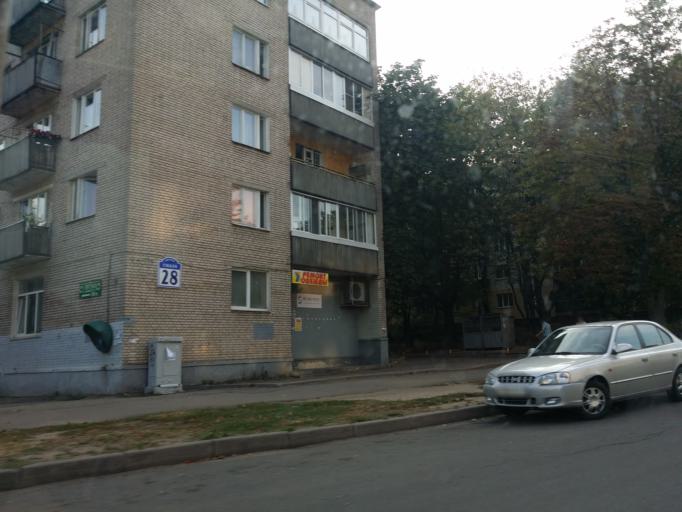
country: BY
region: Minsk
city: Minsk
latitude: 53.9111
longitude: 27.5954
